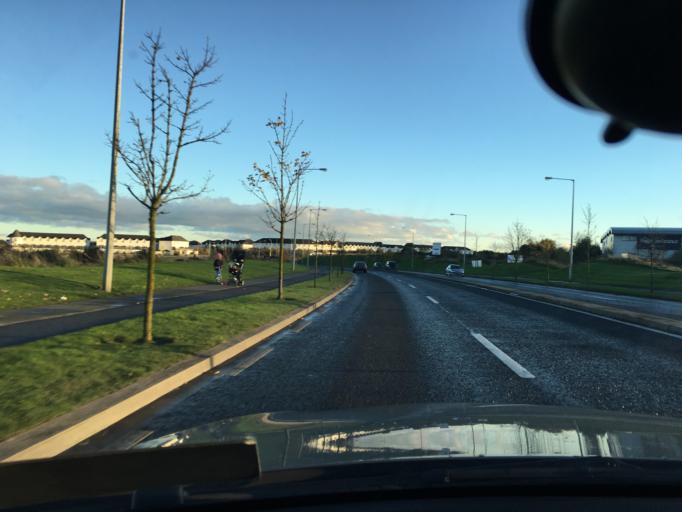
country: IE
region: Leinster
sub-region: Fingal County
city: Swords
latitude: 53.4458
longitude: -6.2185
